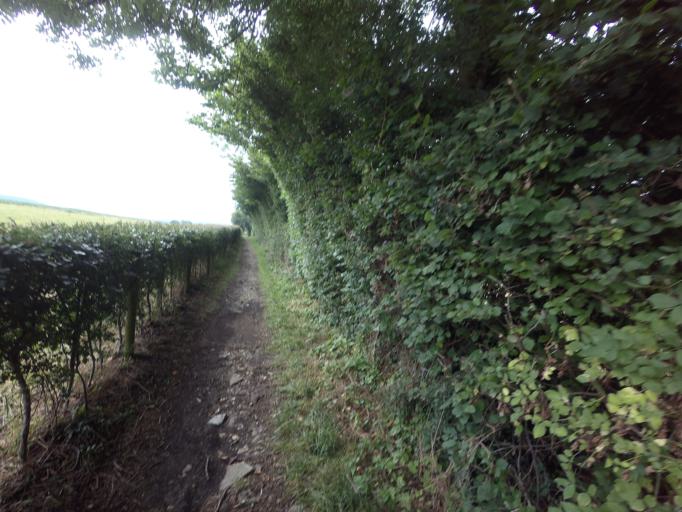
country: NL
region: Limburg
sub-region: Gemeente Simpelveld
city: Simpelveld
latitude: 50.7951
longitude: 5.9598
